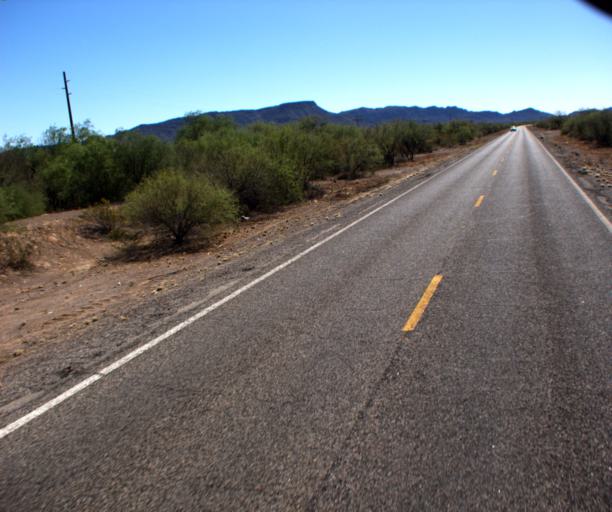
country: US
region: Arizona
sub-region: Pima County
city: Ajo
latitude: 32.3276
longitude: -112.7789
